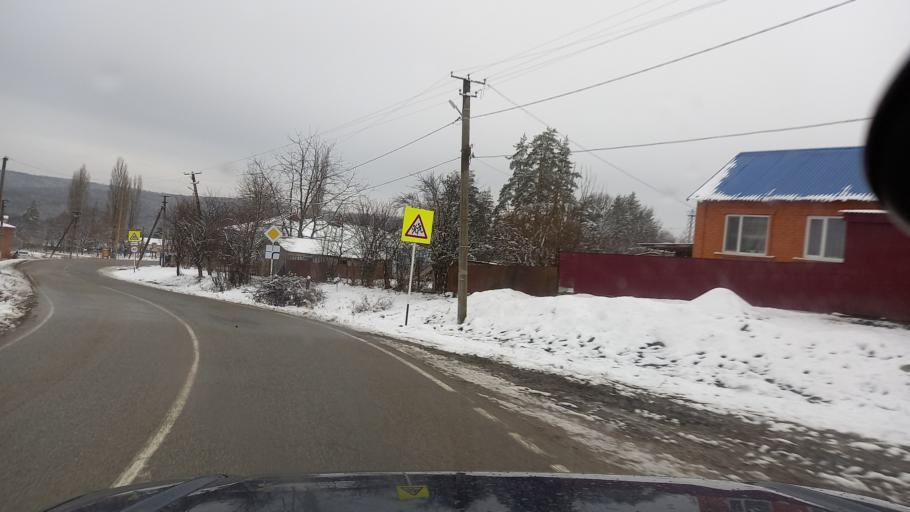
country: RU
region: Adygeya
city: Abadzekhskaya
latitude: 44.3551
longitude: 40.4084
